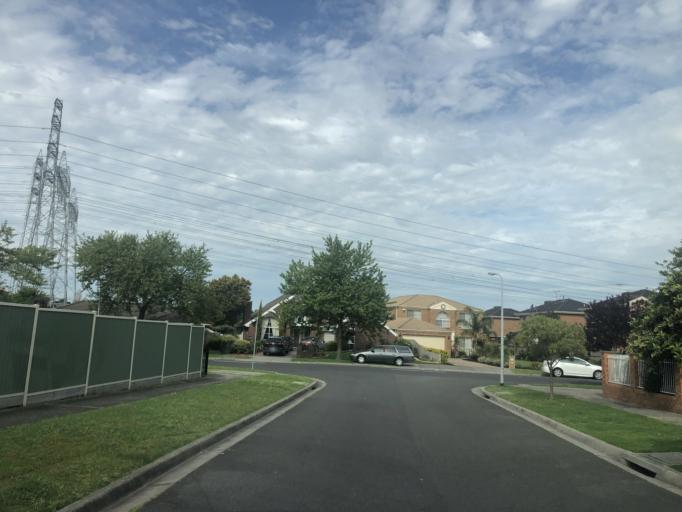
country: AU
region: Victoria
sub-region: Casey
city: Hallam
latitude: -38.0133
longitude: 145.2826
